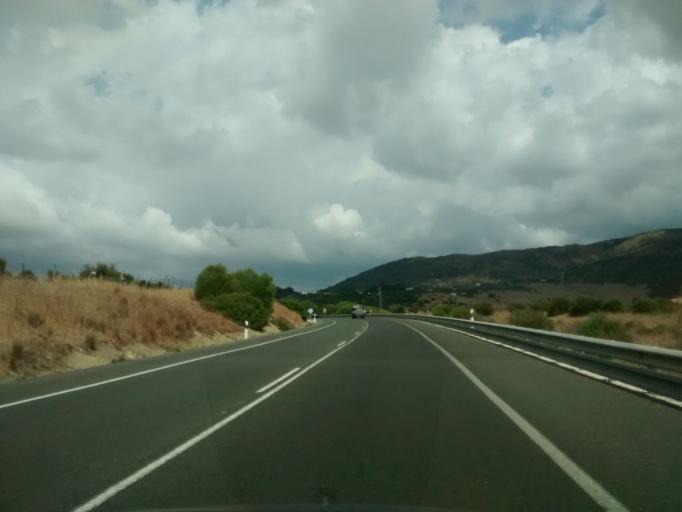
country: ES
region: Andalusia
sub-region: Provincia de Cadiz
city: Zahara de los Atunes
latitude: 36.1178
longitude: -5.7074
